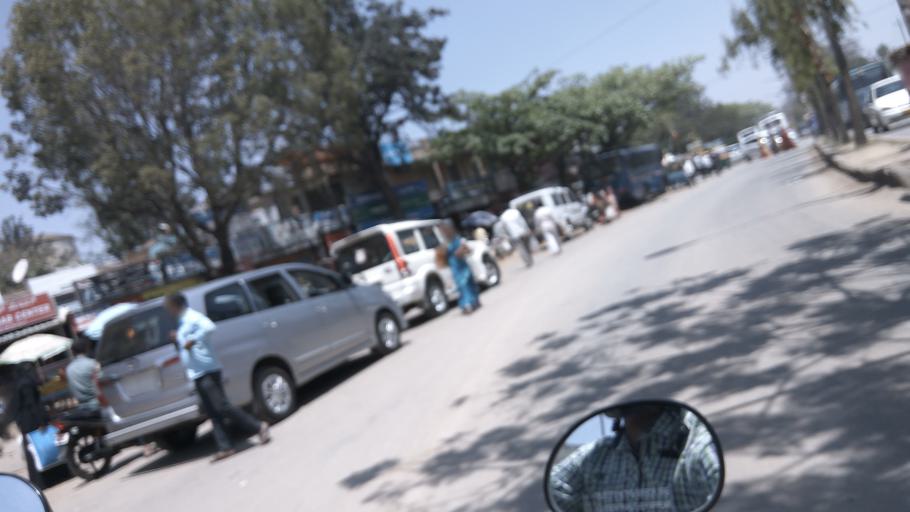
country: IN
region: Karnataka
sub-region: Kolar
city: Mulbagal
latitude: 13.1642
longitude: 78.3941
